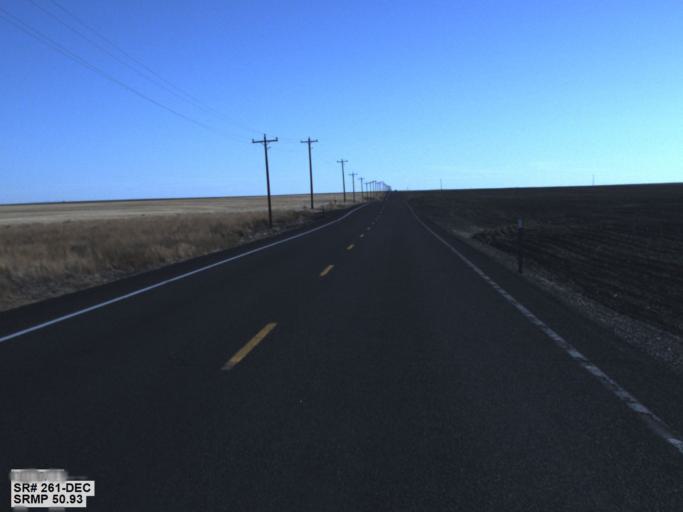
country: US
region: Washington
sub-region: Adams County
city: Ritzville
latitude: 46.9508
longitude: -118.3434
